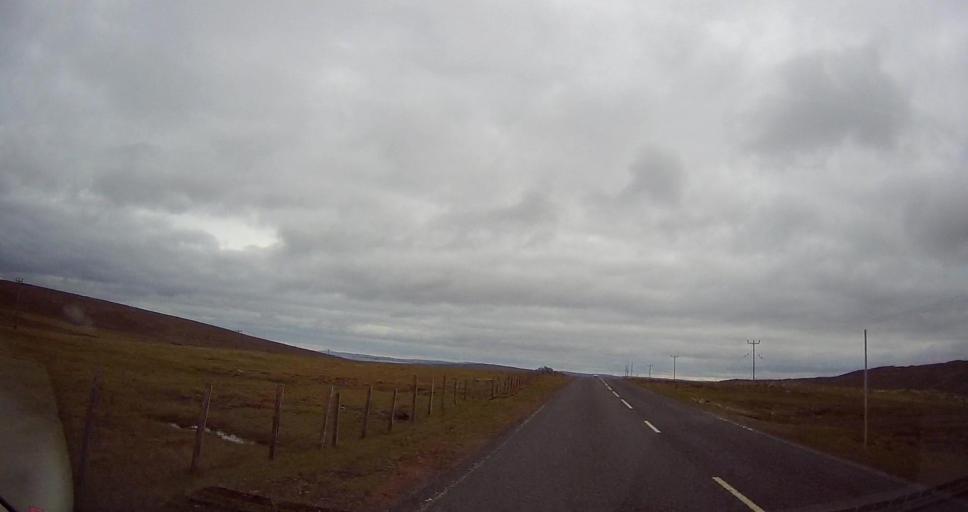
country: GB
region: Scotland
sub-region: Shetland Islands
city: Shetland
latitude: 60.7297
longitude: -0.8979
